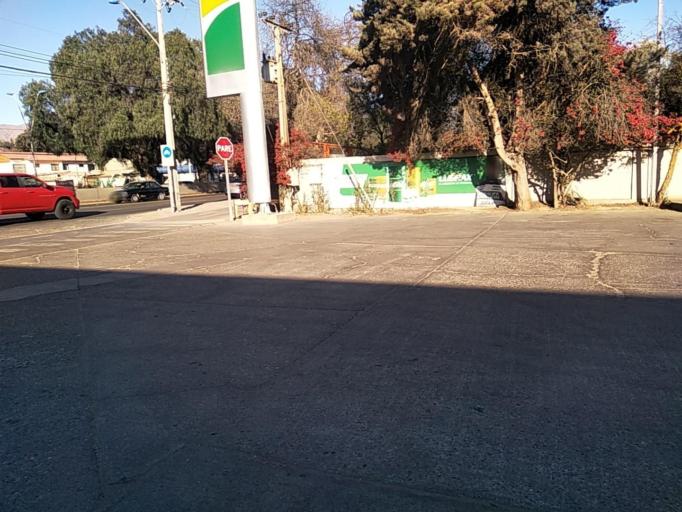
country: CL
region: Atacama
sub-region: Provincia de Copiapo
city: Copiapo
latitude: -27.3640
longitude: -70.3439
